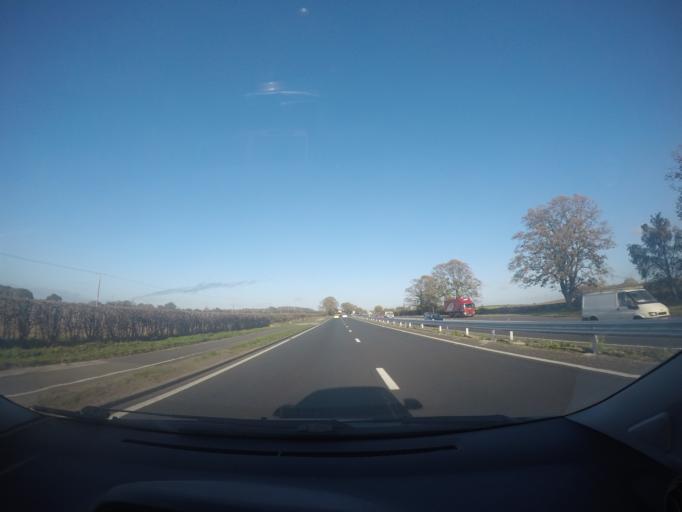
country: GB
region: England
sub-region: City of York
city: Askham Richard
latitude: 53.8969
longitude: -1.2080
